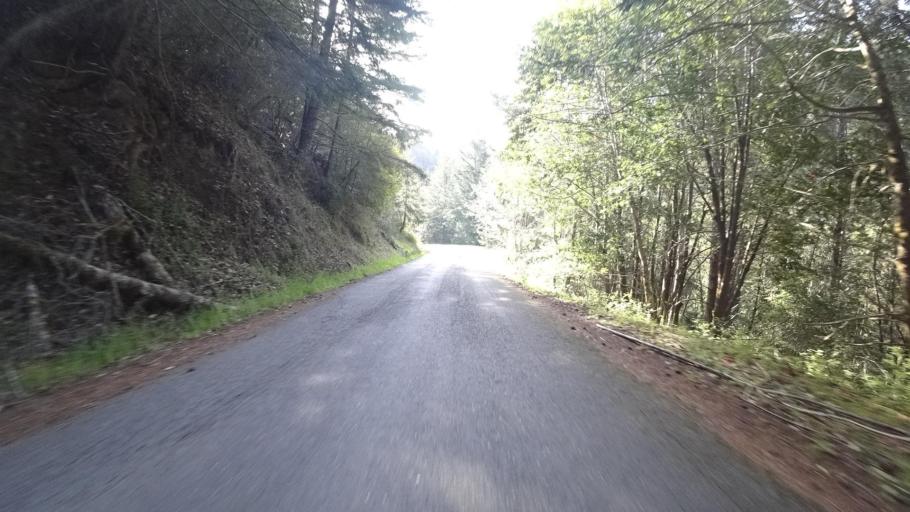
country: US
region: California
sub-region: Humboldt County
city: Bayside
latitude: 40.6978
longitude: -123.9402
